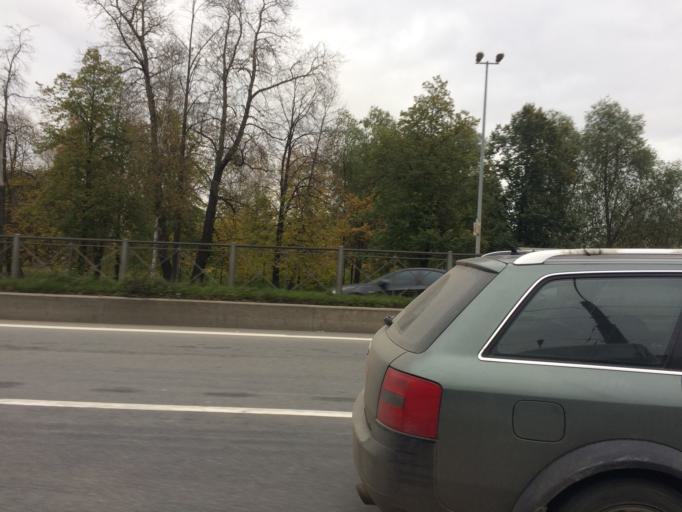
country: RU
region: Leningrad
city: Rybatskoye
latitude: 59.8483
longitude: 30.4825
